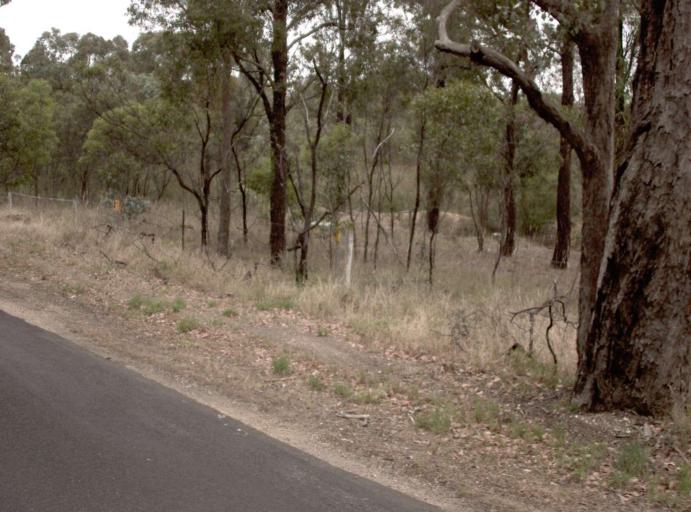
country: AU
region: Victoria
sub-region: Wellington
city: Heyfield
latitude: -37.9620
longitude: 146.7746
